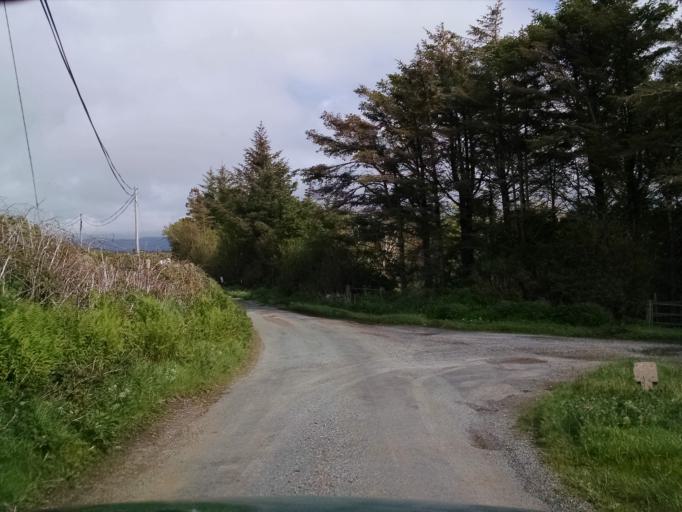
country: IE
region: Connaught
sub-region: County Galway
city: Clifden
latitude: 53.7599
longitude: -9.8430
